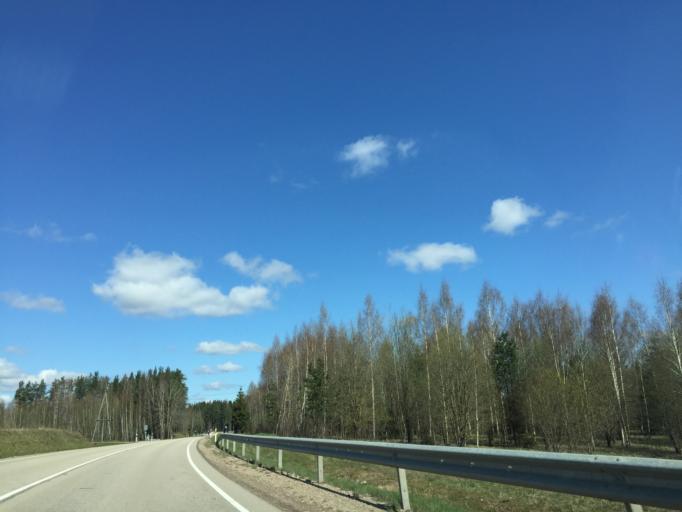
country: LV
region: Rezekne
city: Rezekne
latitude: 56.5614
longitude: 27.2736
